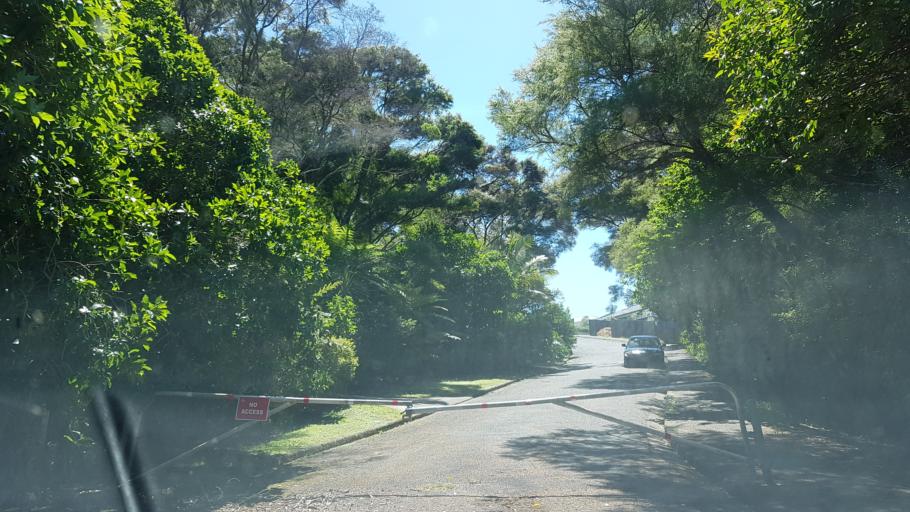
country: NZ
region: Auckland
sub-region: Auckland
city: North Shore
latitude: -36.8051
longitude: 174.7410
